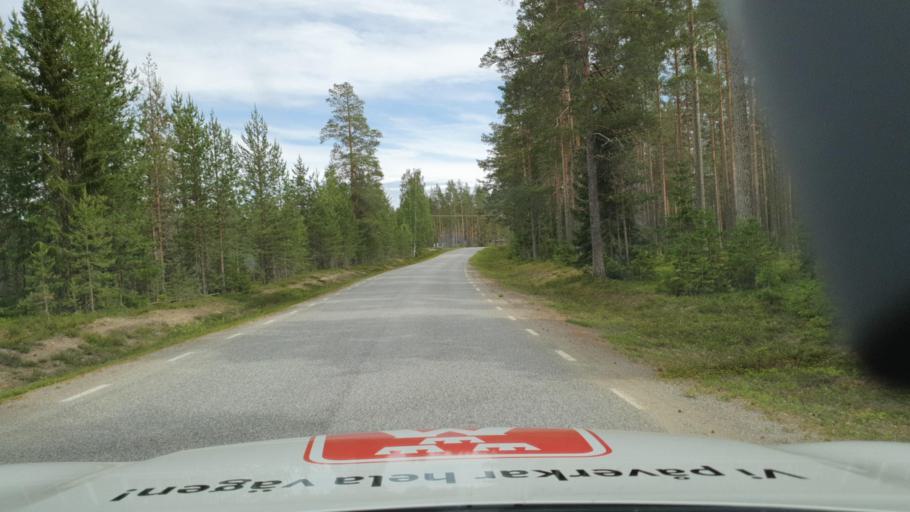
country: SE
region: Vaesterbotten
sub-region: Skelleftea Kommun
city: Burtraesk
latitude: 64.5008
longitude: 20.8448
